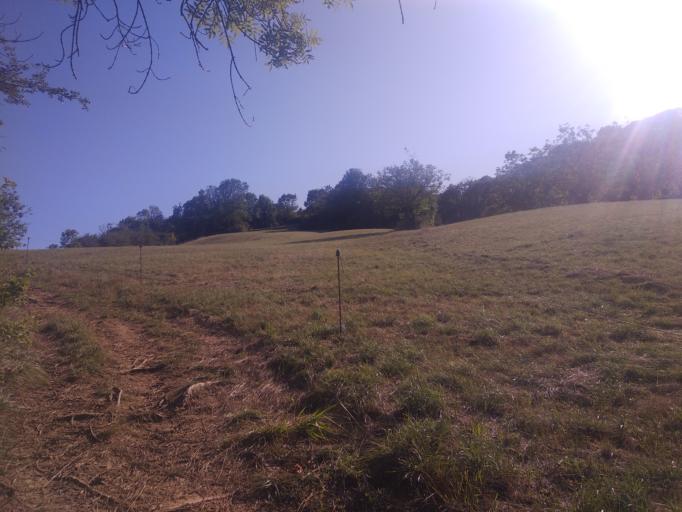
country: FR
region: Rhone-Alpes
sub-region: Departement de l'Ardeche
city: Vernosc-les-Annonay
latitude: 45.1888
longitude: 4.7439
